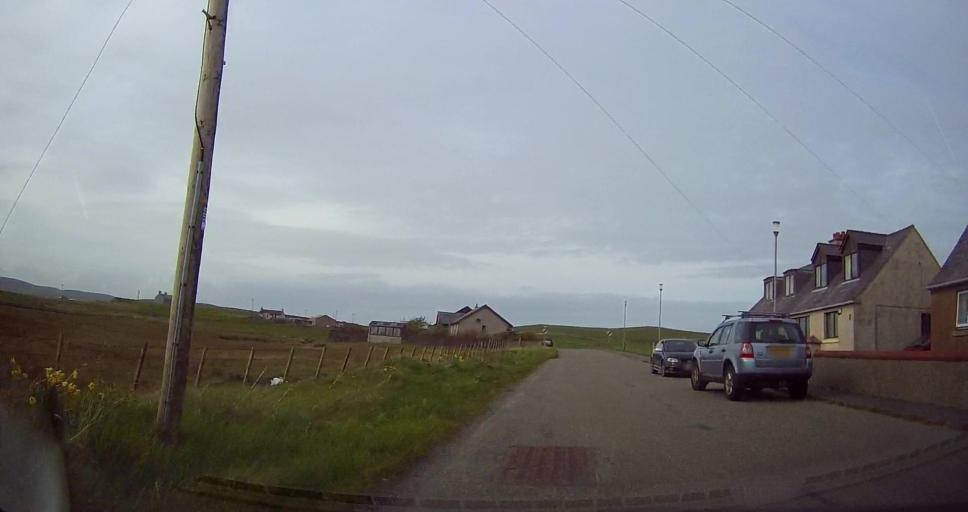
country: GB
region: Scotland
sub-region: Shetland Islands
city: Shetland
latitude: 60.1546
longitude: -1.1158
